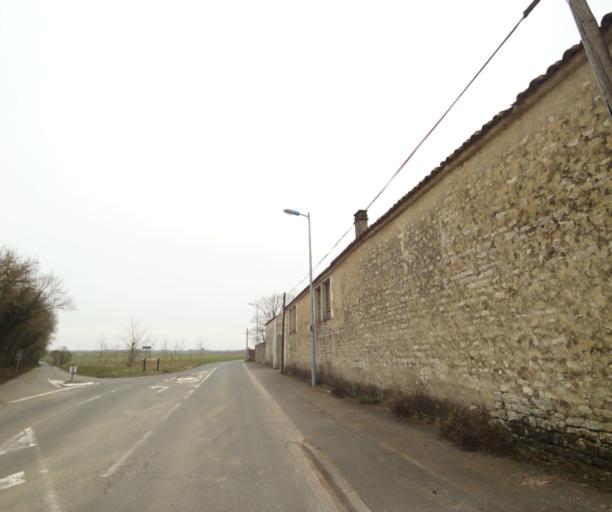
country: FR
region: Poitou-Charentes
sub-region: Departement des Deux-Sevres
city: Magne
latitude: 46.3309
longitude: -0.5206
